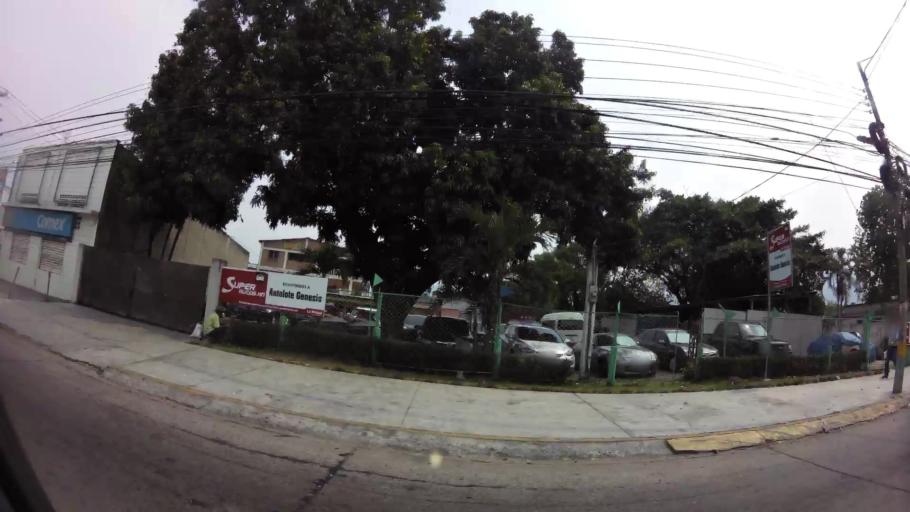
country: HN
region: Cortes
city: San Pedro Sula
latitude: 15.4908
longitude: -88.0298
